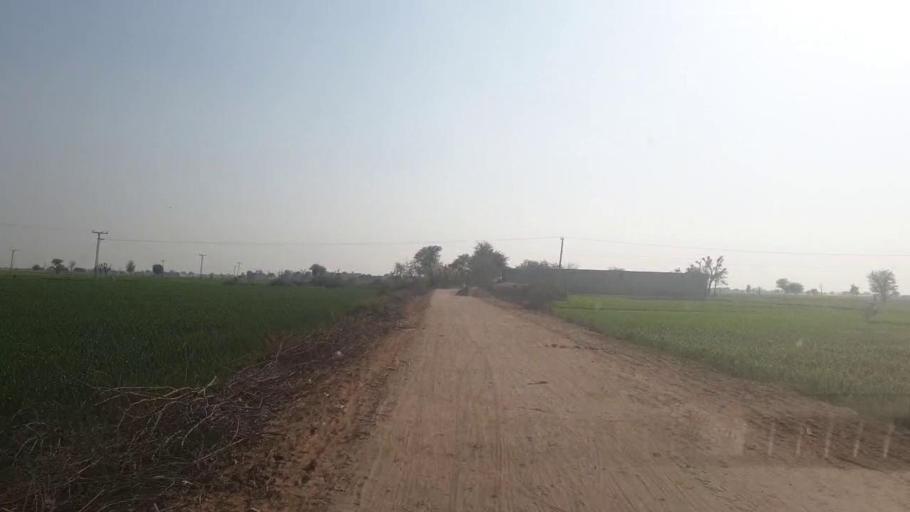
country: PK
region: Sindh
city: Sakrand
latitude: 26.0655
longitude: 68.3814
